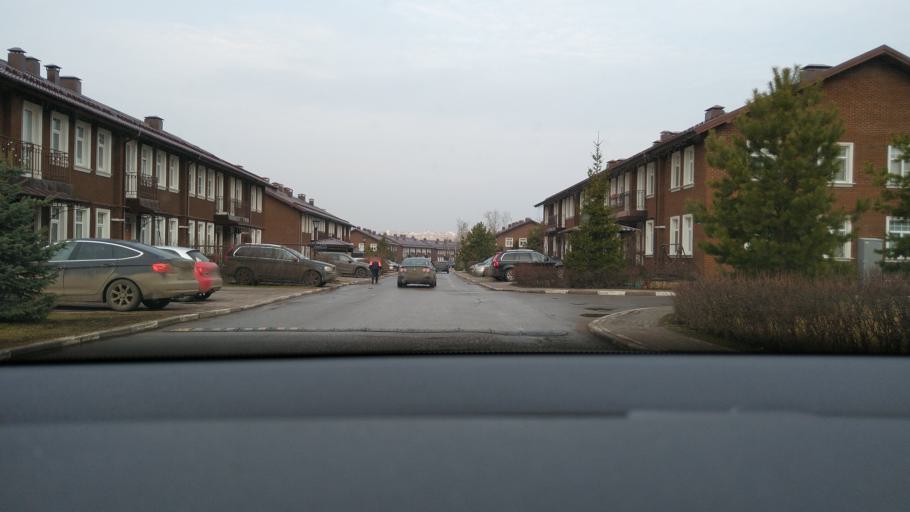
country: RU
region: Moskovskaya
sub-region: Leninskiy Rayon
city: Vnukovo
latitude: 55.6112
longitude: 37.3259
